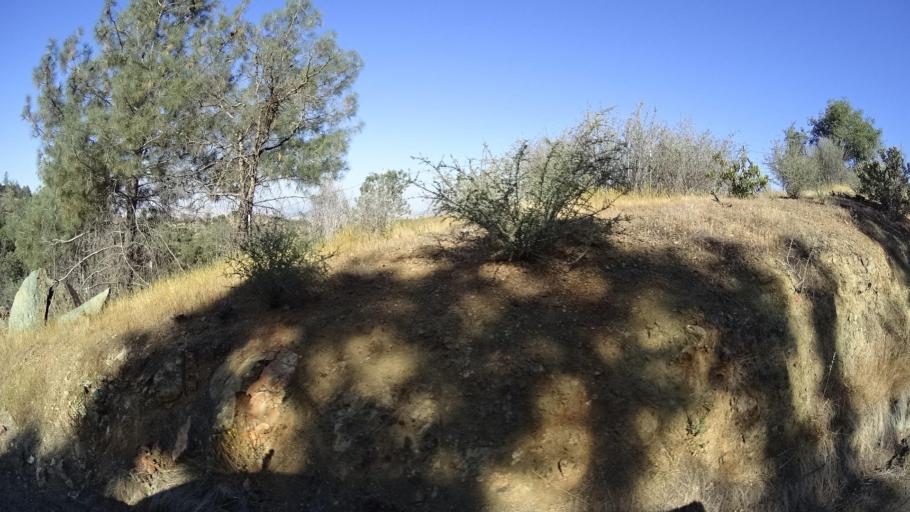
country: US
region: California
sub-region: Mariposa County
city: Mariposa
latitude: 37.5661
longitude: -120.1571
